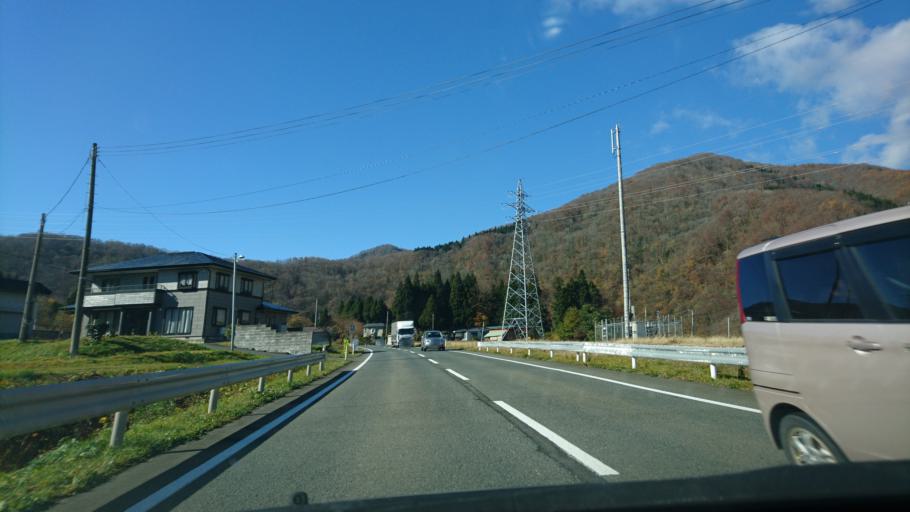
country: JP
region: Iwate
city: Kitakami
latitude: 39.3097
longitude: 140.9076
